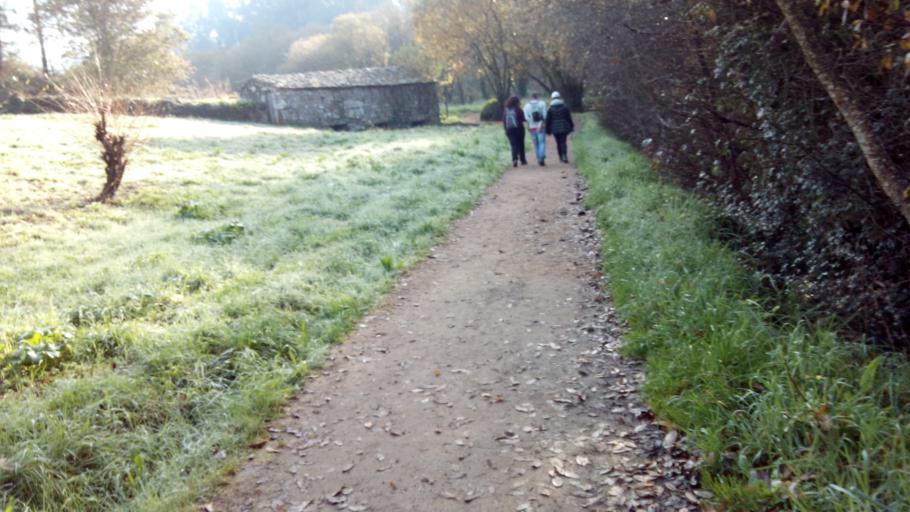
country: ES
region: Galicia
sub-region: Provincia de Pontevedra
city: Meis
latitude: 42.4919
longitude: -8.7565
